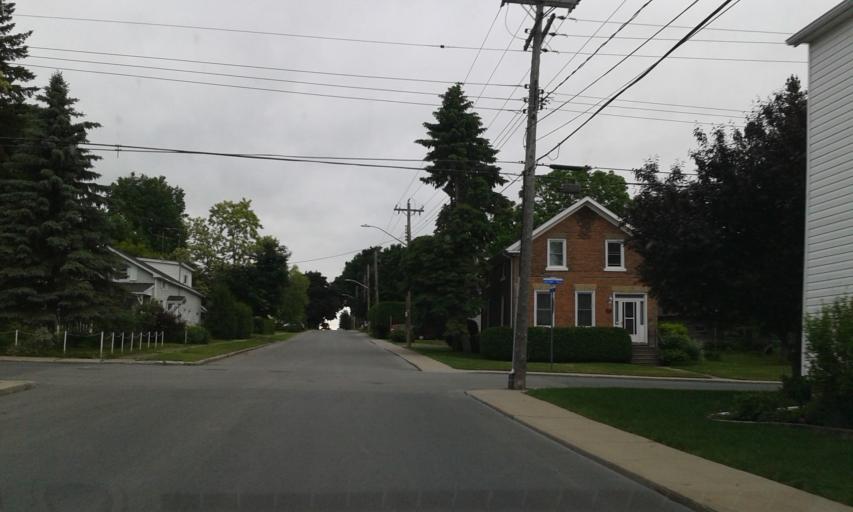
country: CA
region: Ontario
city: Prescott
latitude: 44.7058
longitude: -75.5216
